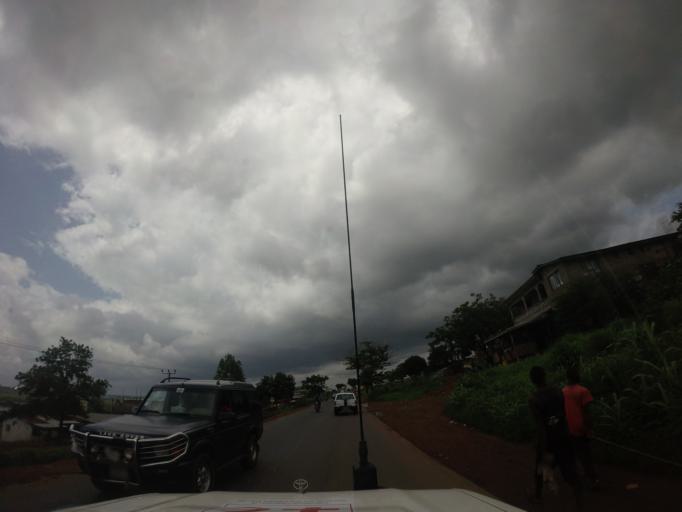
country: SL
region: Western Area
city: Waterloo
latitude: 8.3545
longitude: -13.0796
